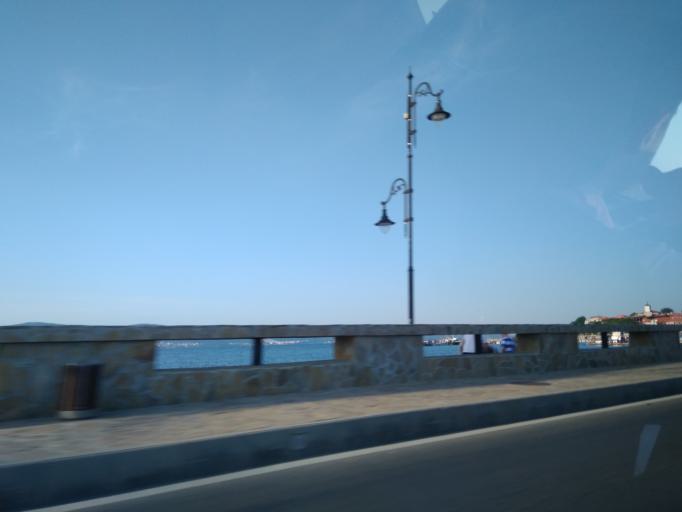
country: BG
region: Burgas
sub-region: Obshtina Nesebur
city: Nesebar
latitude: 42.6592
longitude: 27.7286
